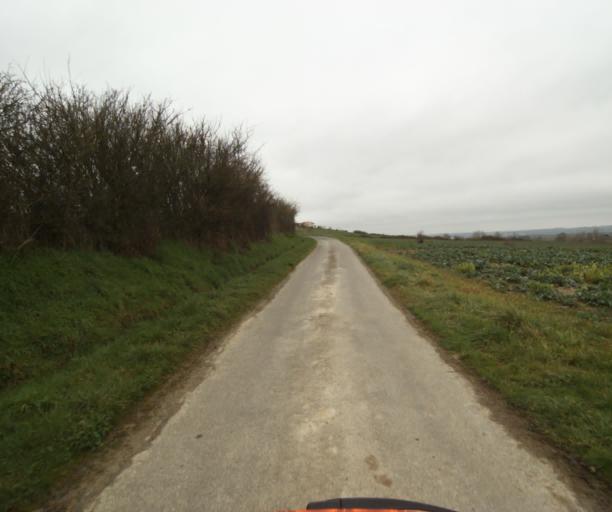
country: FR
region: Midi-Pyrenees
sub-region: Departement de la Haute-Garonne
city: Gaillac-Toulza
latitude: 43.2575
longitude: 1.5197
